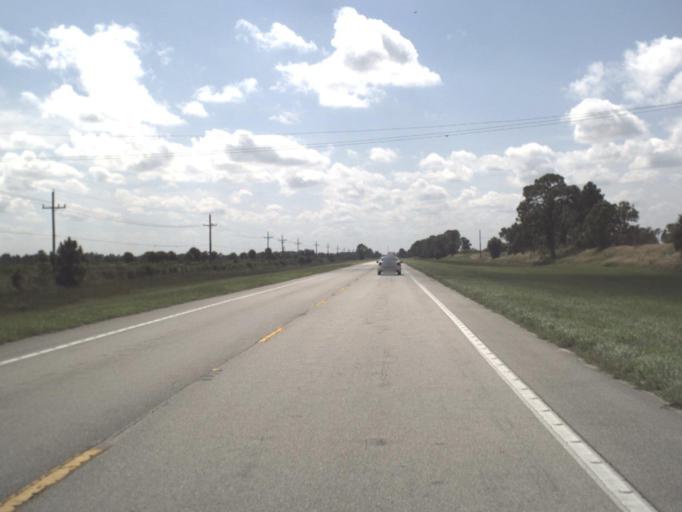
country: US
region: Florida
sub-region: Hendry County
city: Port LaBelle
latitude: 26.6266
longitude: -81.4365
